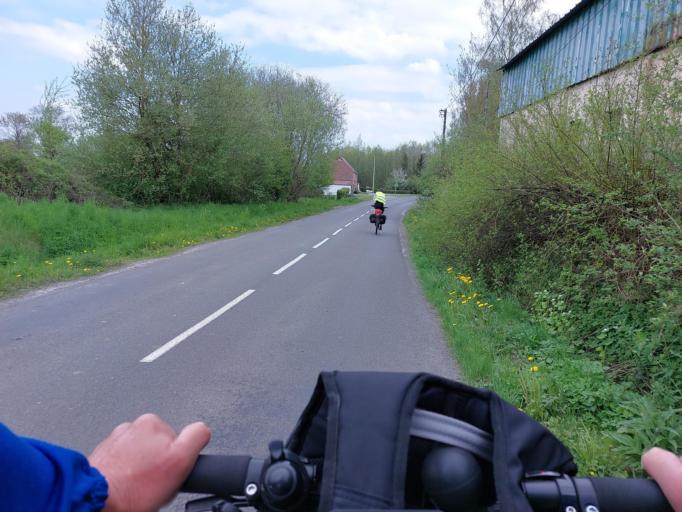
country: FR
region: Nord-Pas-de-Calais
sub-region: Departement du Nord
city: La Longueville
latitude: 50.2768
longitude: 3.8774
